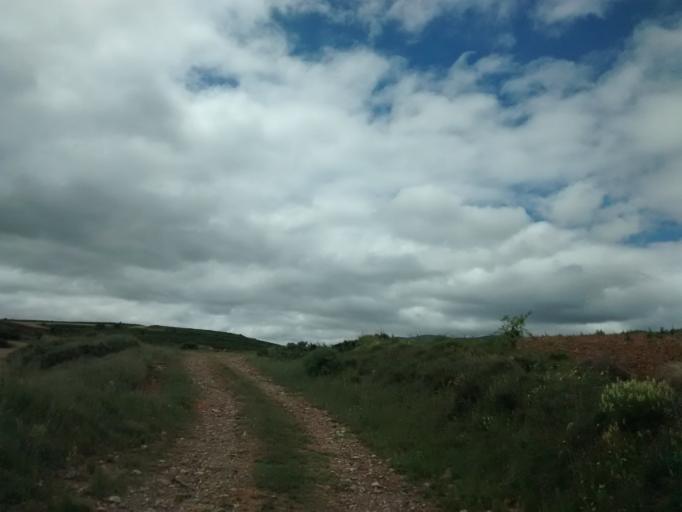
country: ES
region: Aragon
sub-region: Provincia de Zaragoza
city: Trasmoz
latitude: 41.8397
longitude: -1.7378
